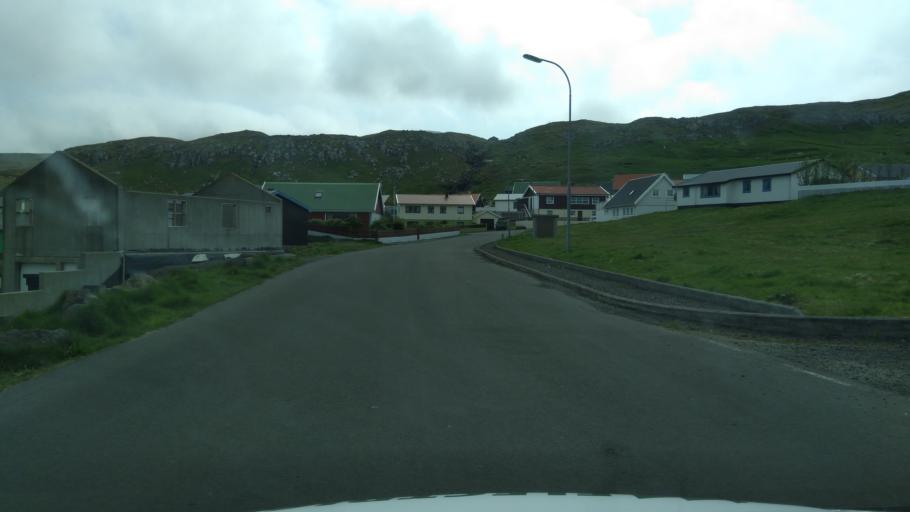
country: FO
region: Sandoy
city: Sandur
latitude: 61.9041
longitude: -6.8882
